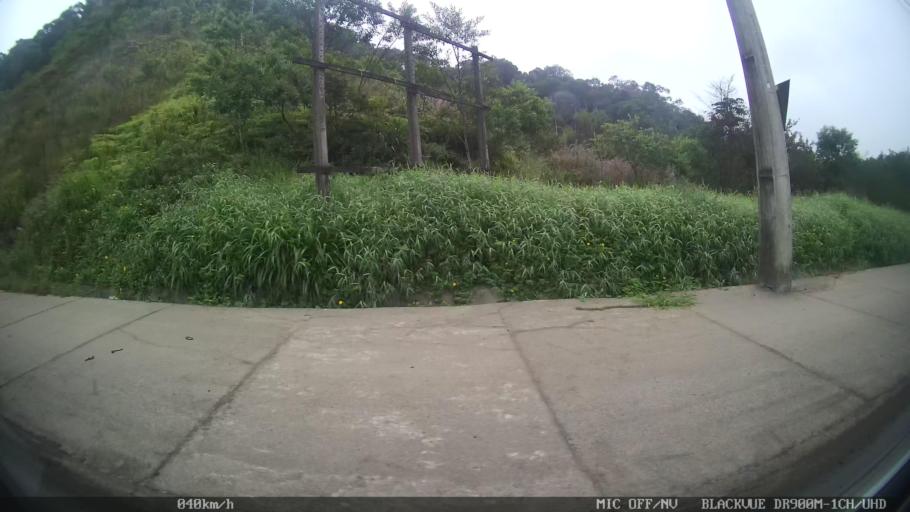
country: BR
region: Santa Catarina
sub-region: Joinville
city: Joinville
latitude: -26.2350
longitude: -48.8194
